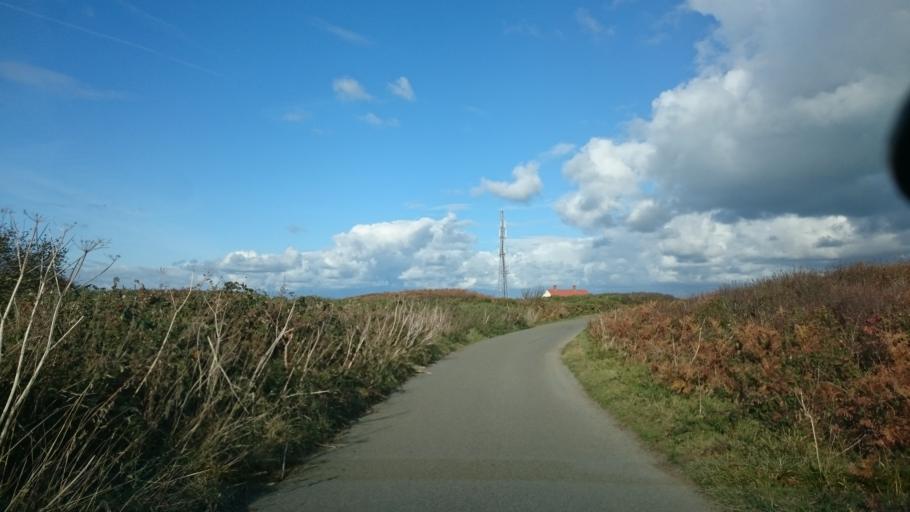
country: GG
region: St Peter Port
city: Saint Peter Port
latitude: 49.4283
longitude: -2.6676
